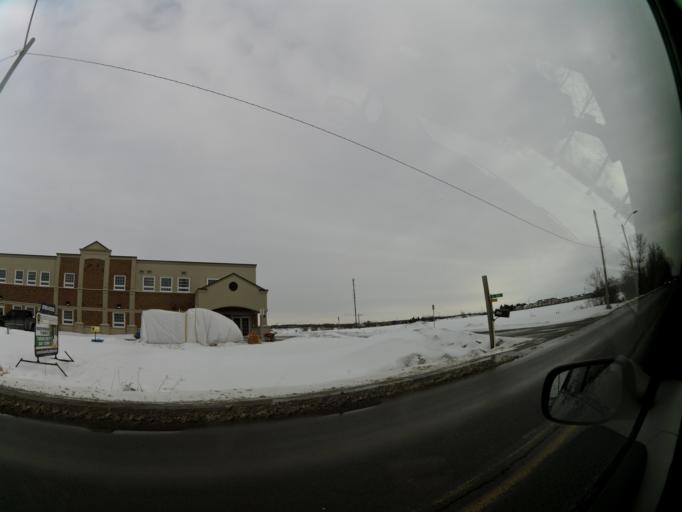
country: CA
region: Ontario
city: Bells Corners
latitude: 45.2921
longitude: -75.9245
